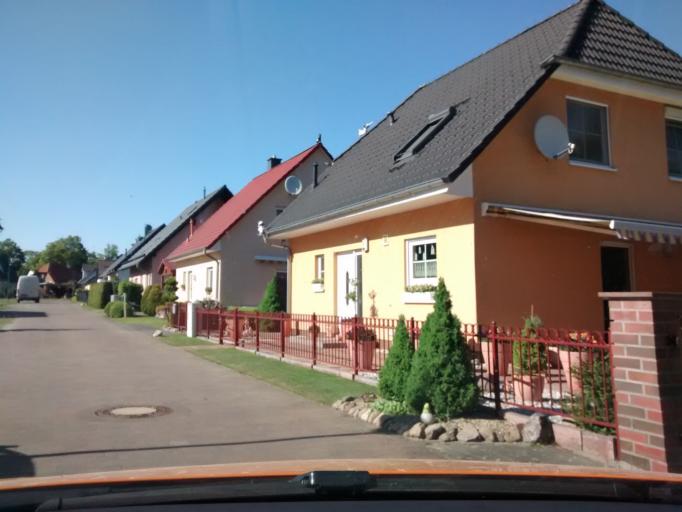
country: DE
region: Brandenburg
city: Bad Saarow
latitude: 52.2651
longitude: 14.0716
